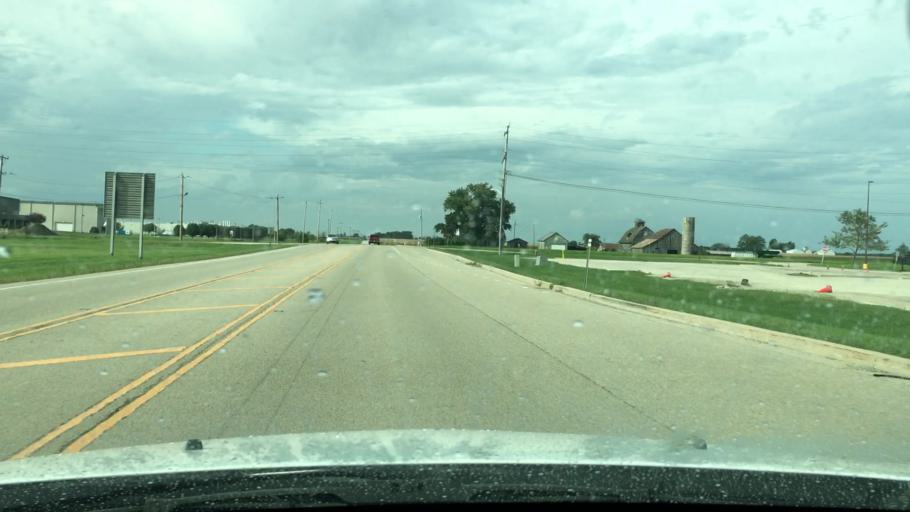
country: US
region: Illinois
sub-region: LaSalle County
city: Peru
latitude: 41.3733
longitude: -89.1255
